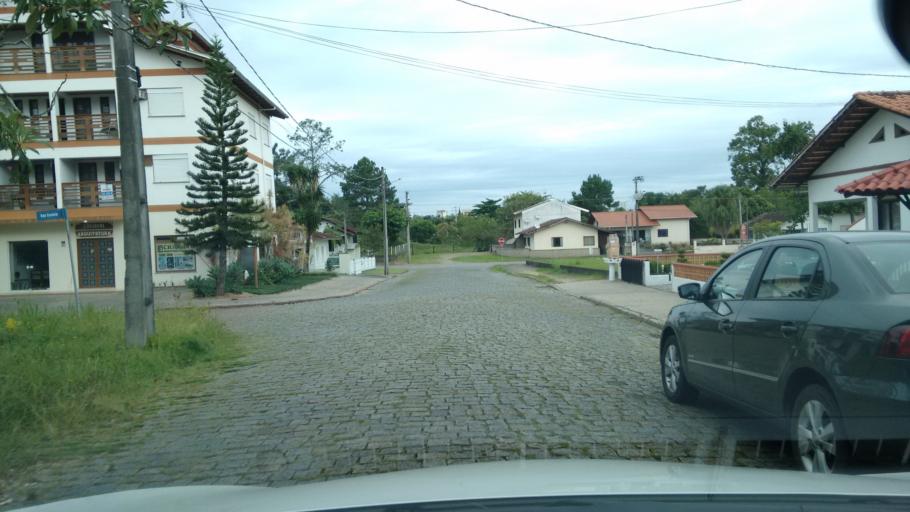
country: BR
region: Santa Catarina
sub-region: Timbo
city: Timbo
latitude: -26.8134
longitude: -49.2698
